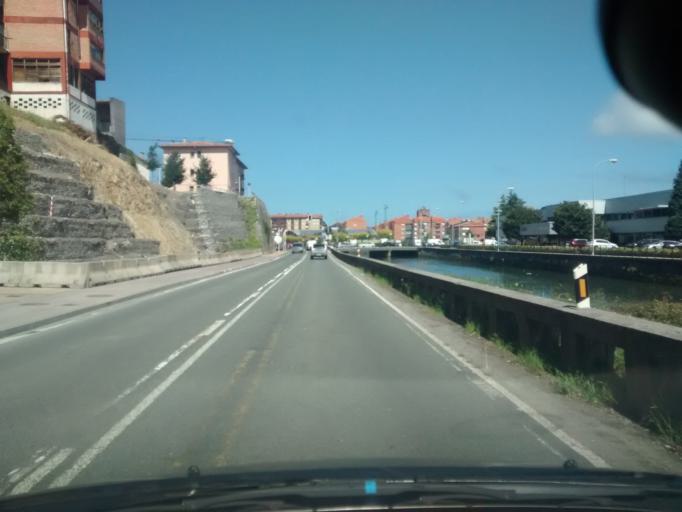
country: ES
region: Basque Country
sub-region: Provincia de Guipuzcoa
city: Zumaia
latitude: 43.2884
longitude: -2.2591
